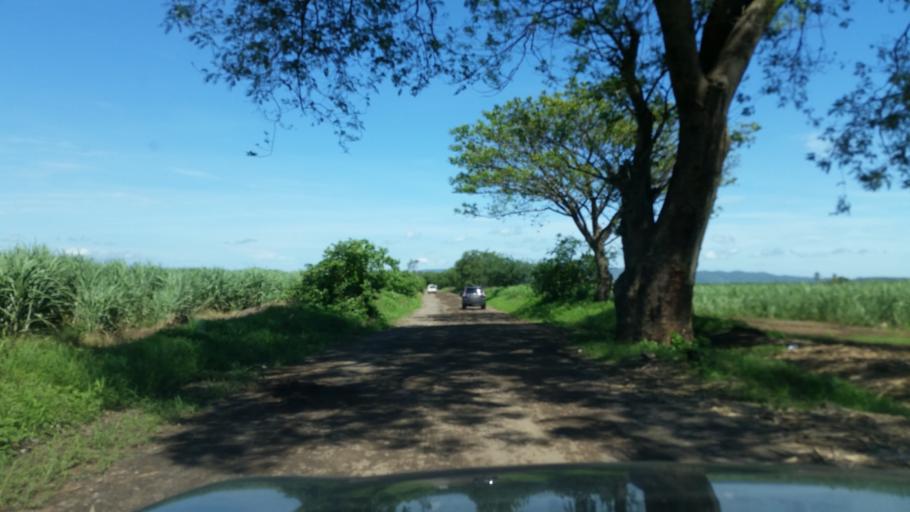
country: NI
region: Chinandega
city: Puerto Morazan
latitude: 12.7742
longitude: -87.1042
